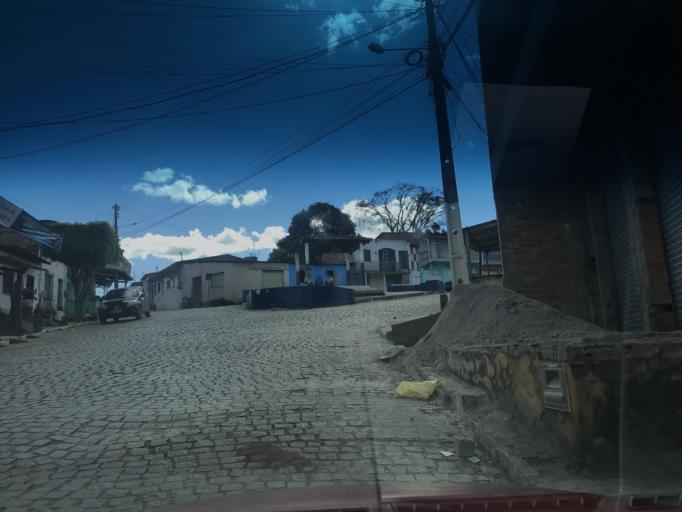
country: BR
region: Bahia
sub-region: Gandu
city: Gandu
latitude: -13.7457
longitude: -39.4922
